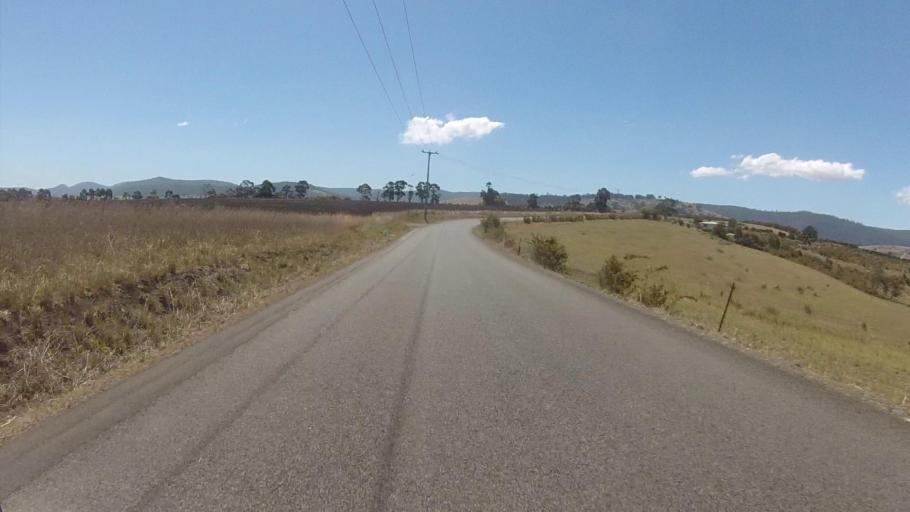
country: AU
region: Tasmania
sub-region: Sorell
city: Sorell
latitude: -42.7763
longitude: 147.5806
